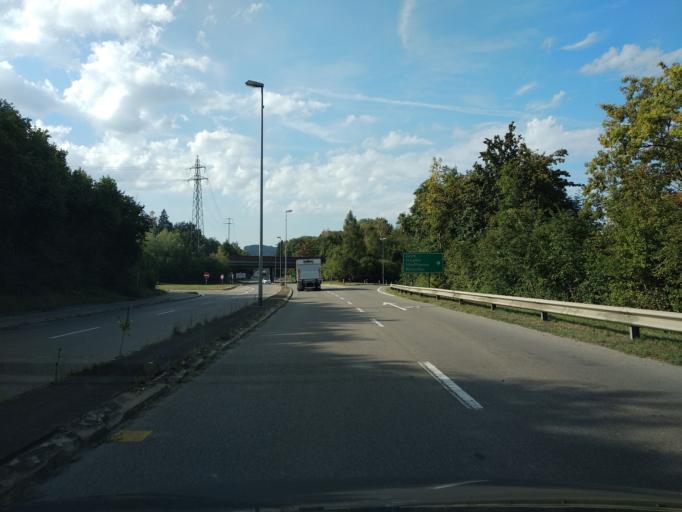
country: CH
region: Thurgau
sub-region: Frauenfeld District
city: Frauenfeld
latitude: 47.5623
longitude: 8.8703
